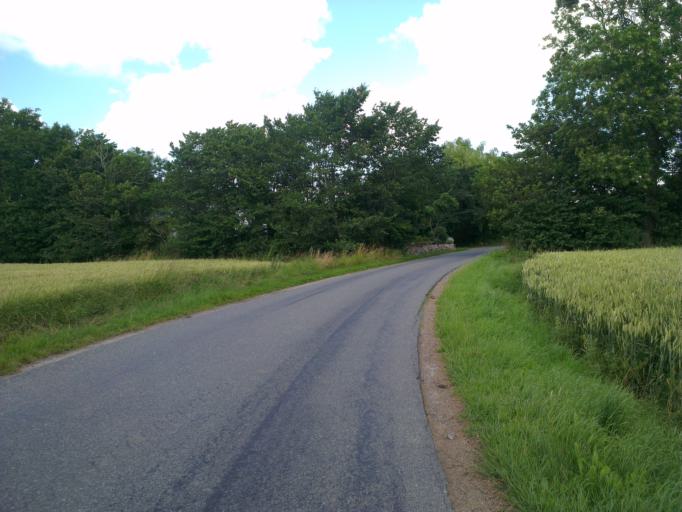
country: DK
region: Capital Region
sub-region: Frederikssund Kommune
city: Skibby
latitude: 55.7472
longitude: 12.0194
